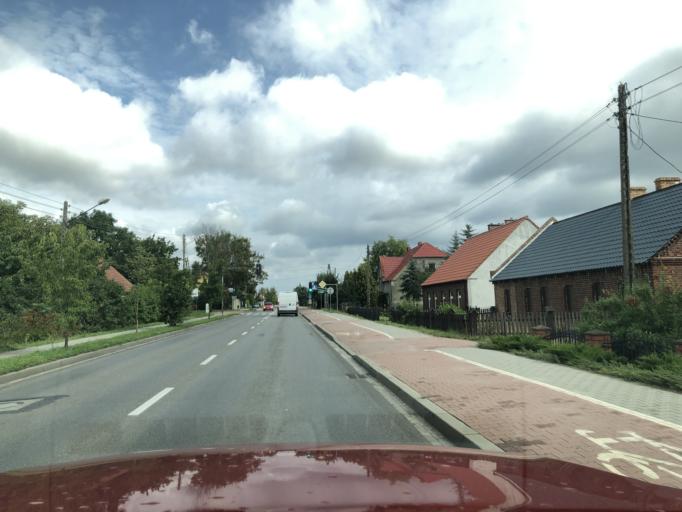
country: PL
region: Greater Poland Voivodeship
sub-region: Powiat szamotulski
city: Pniewy
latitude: 52.5191
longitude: 16.2638
